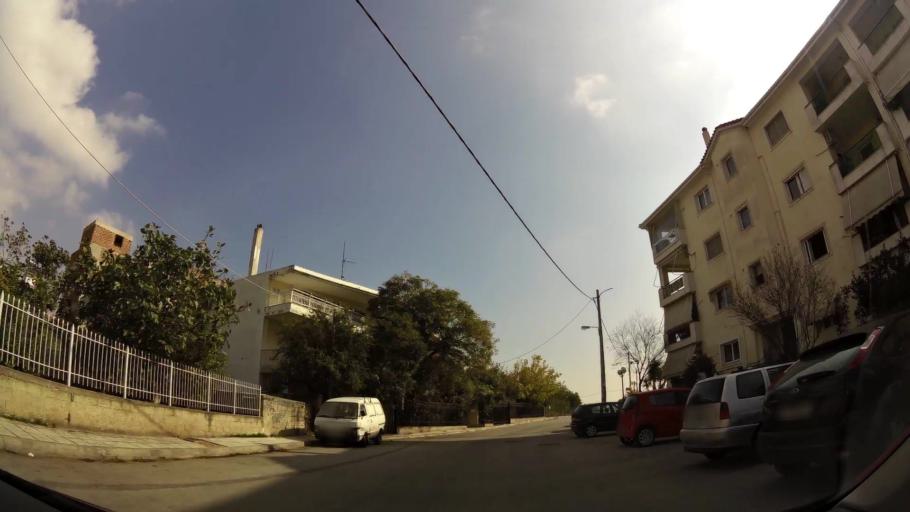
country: GR
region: Attica
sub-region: Nomarchia Dytikis Attikis
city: Zefyri
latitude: 38.0642
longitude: 23.7255
